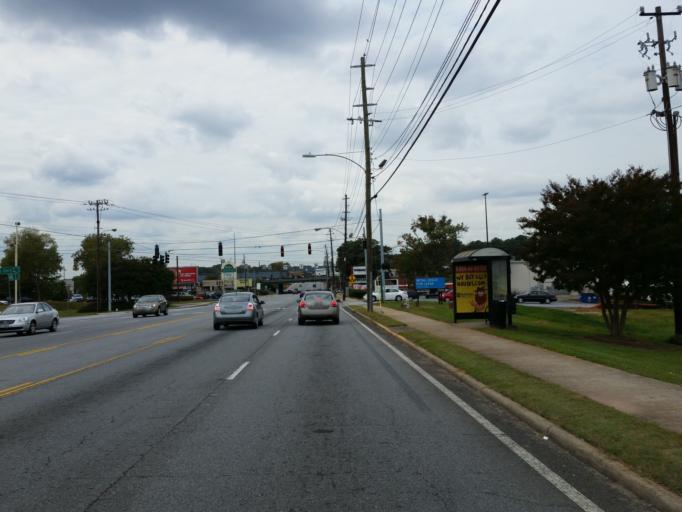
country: US
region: Georgia
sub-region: Cobb County
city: Marietta
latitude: 33.9509
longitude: -84.5124
